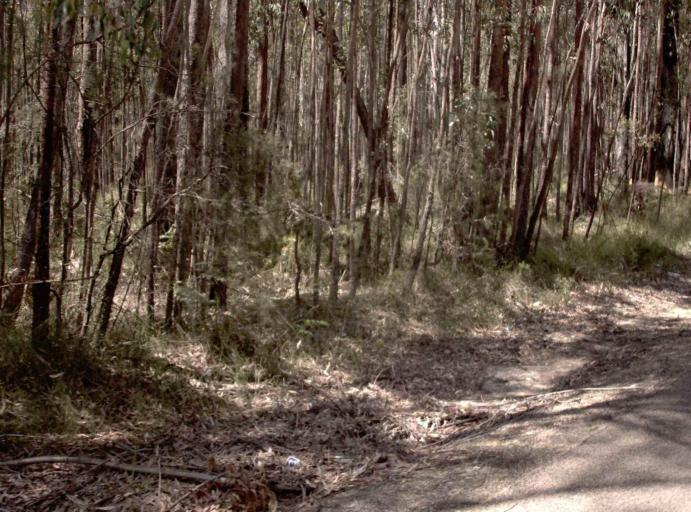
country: AU
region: New South Wales
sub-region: Bombala
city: Bombala
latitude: -37.5729
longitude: 149.2965
